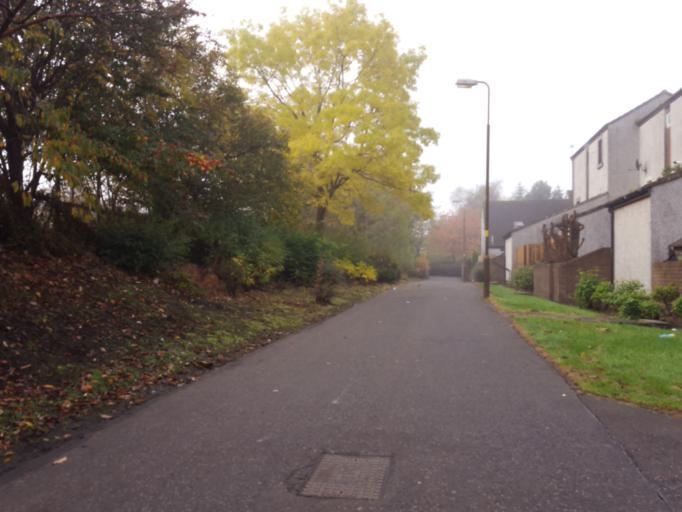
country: GB
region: Scotland
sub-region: West Lothian
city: Livingston
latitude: 55.9034
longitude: -3.5466
